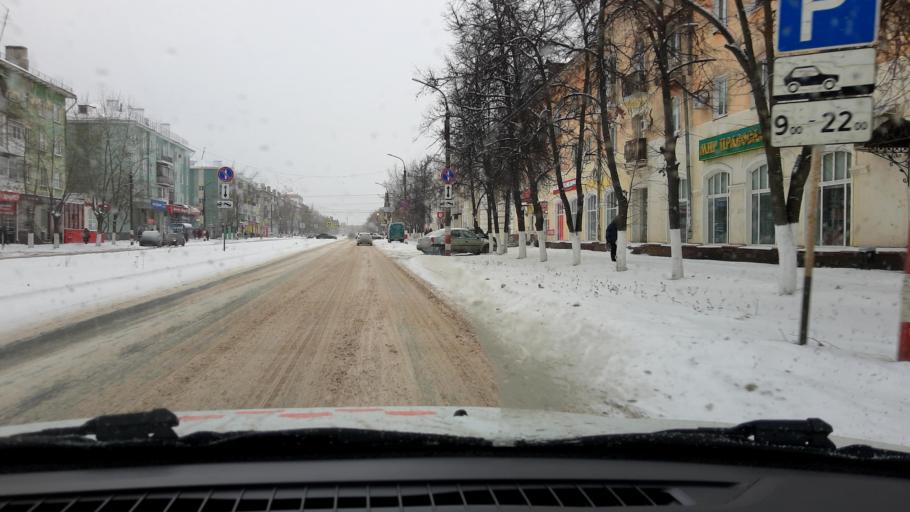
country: RU
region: Nizjnij Novgorod
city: Dzerzhinsk
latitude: 56.2429
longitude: 43.4427
